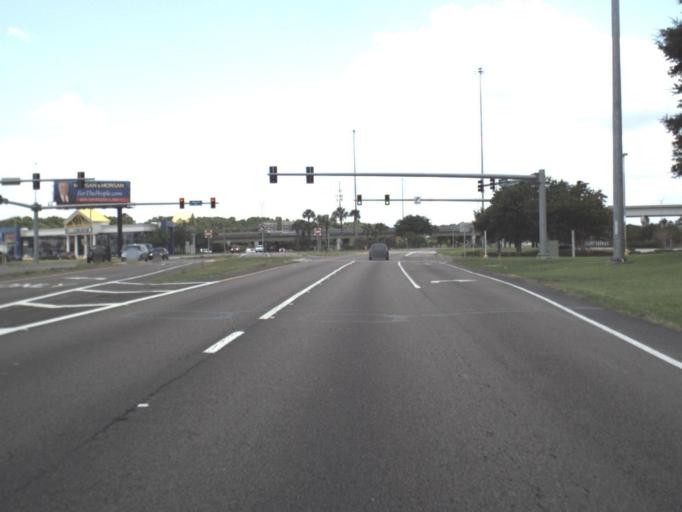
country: US
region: Florida
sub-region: Duval County
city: Jacksonville
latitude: 30.3219
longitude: -81.5548
